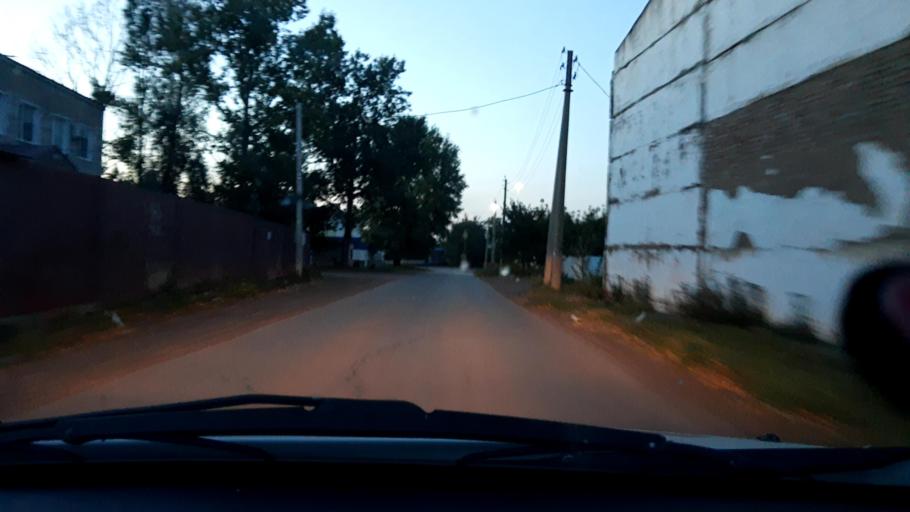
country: RU
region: Bashkortostan
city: Ulukulevo
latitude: 54.4206
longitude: 56.3430
